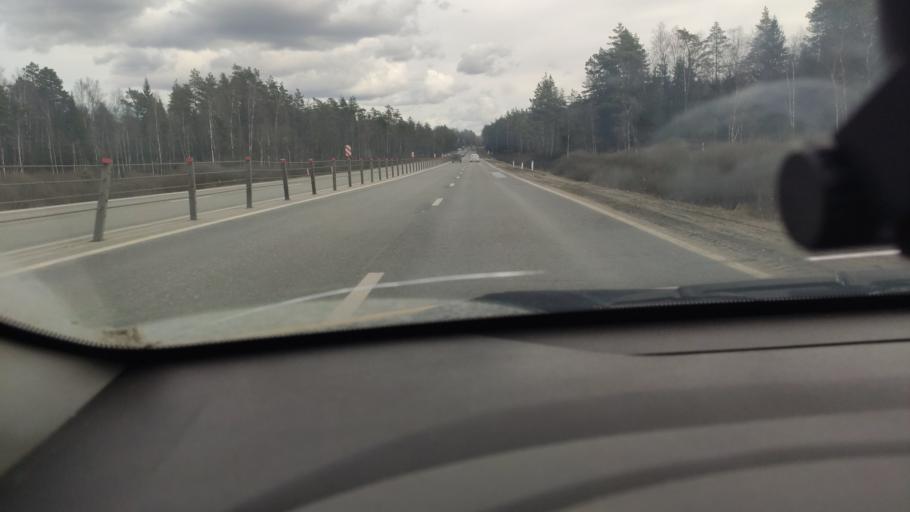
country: RU
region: Moskovskaya
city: Tuchkovo
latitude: 55.5467
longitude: 36.4416
